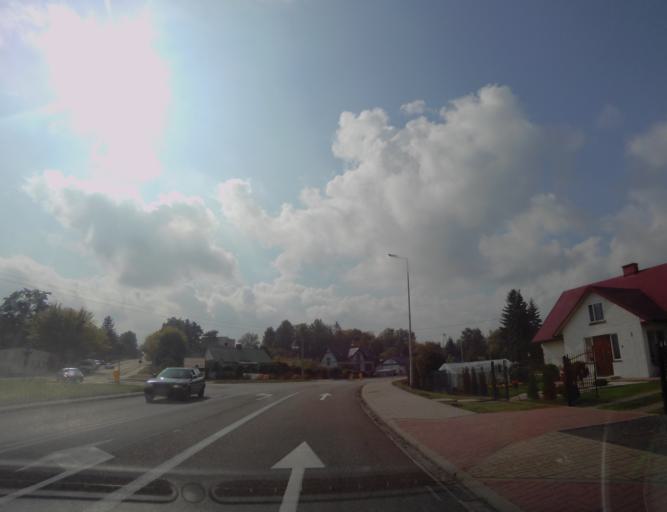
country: PL
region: Lublin Voivodeship
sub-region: Powiat krasnostawski
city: Krasnystaw
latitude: 50.9715
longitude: 23.1602
